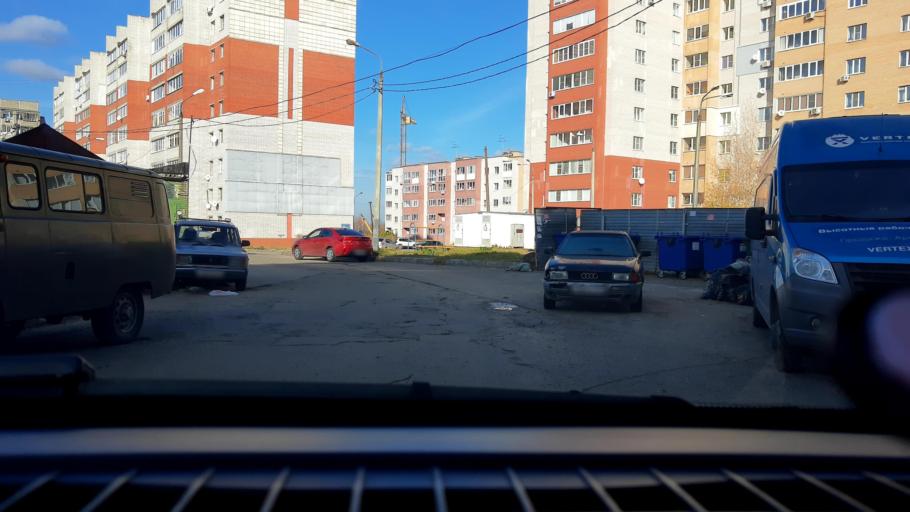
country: RU
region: Nizjnij Novgorod
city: Kstovo
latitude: 56.1592
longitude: 44.2150
